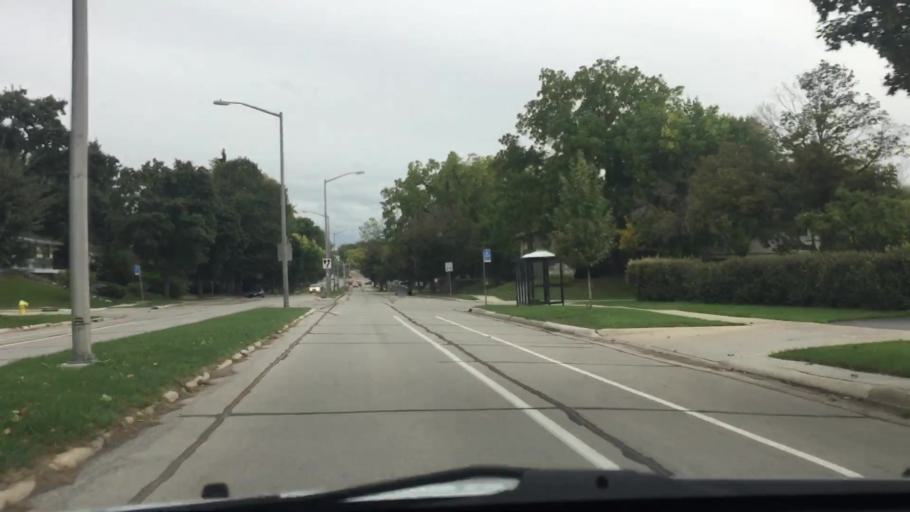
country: US
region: Wisconsin
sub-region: Waukesha County
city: Waukesha
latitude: 42.9921
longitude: -88.2322
